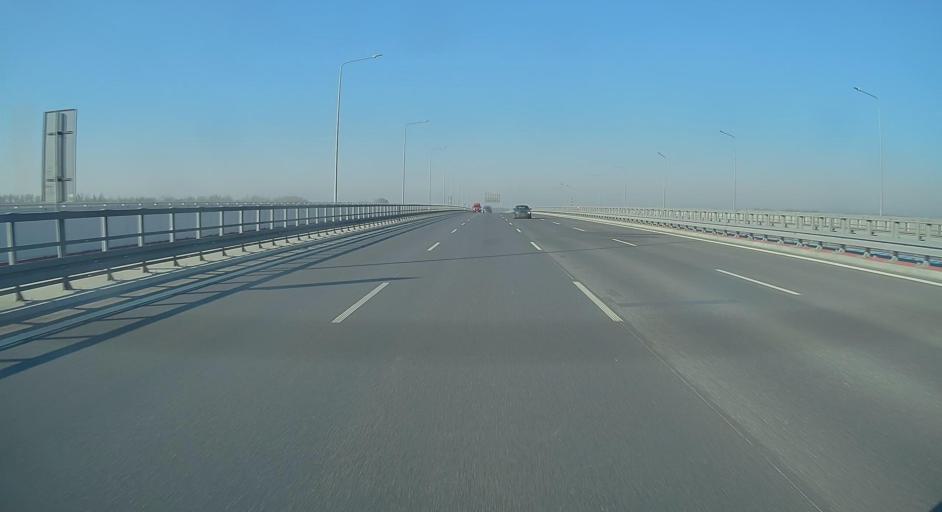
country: PL
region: Masovian Voivodeship
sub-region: Warszawa
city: Wawer
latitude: 52.1624
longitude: 21.1458
